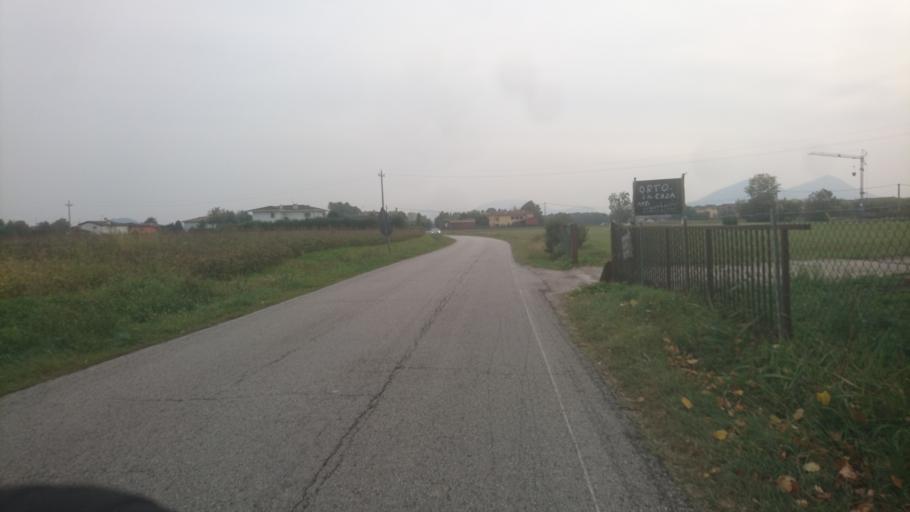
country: IT
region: Veneto
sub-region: Provincia di Padova
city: Saccolongo
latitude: 45.4144
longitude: 11.7294
